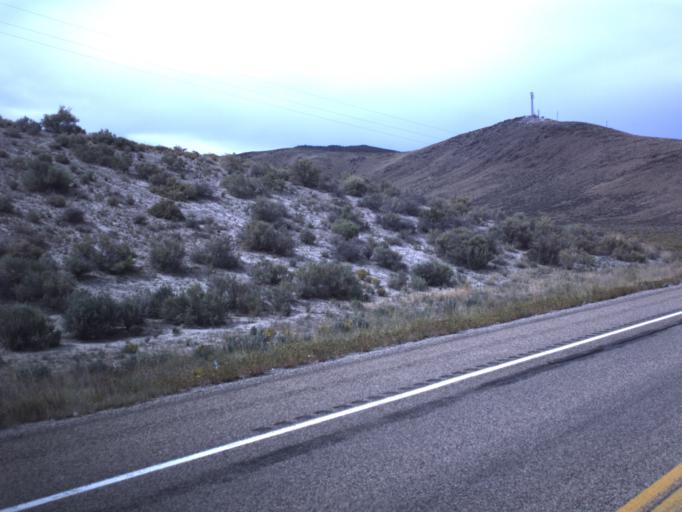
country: US
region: Utah
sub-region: Piute County
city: Junction
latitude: 38.2014
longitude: -112.2321
